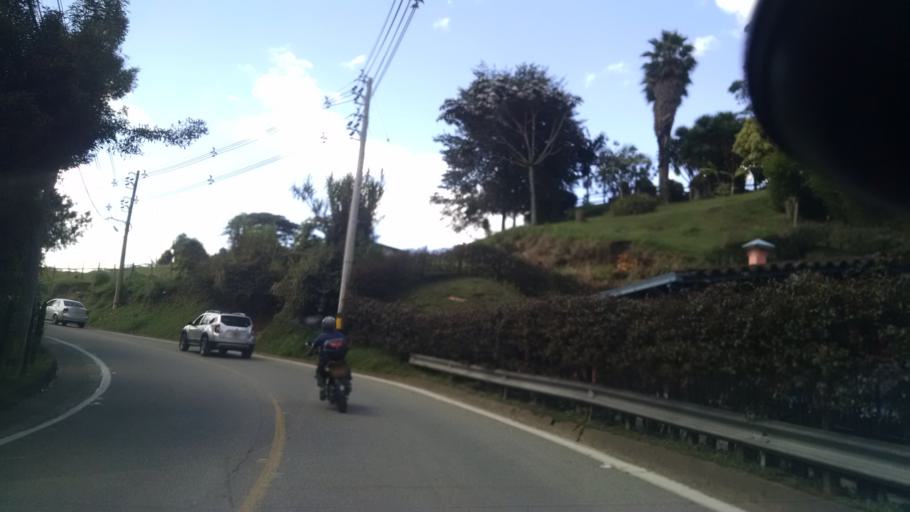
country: CO
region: Antioquia
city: El Retiro
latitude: 6.0751
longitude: -75.4968
